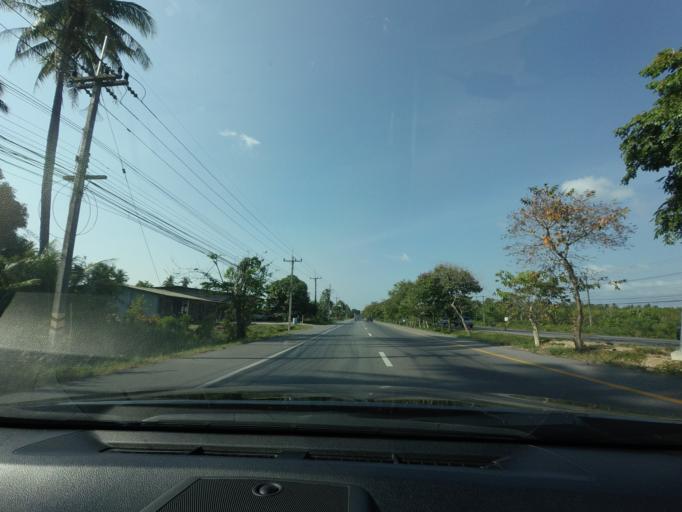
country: TH
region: Prachuap Khiri Khan
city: Prachuap Khiri Khan
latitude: 11.7638
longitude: 99.7686
